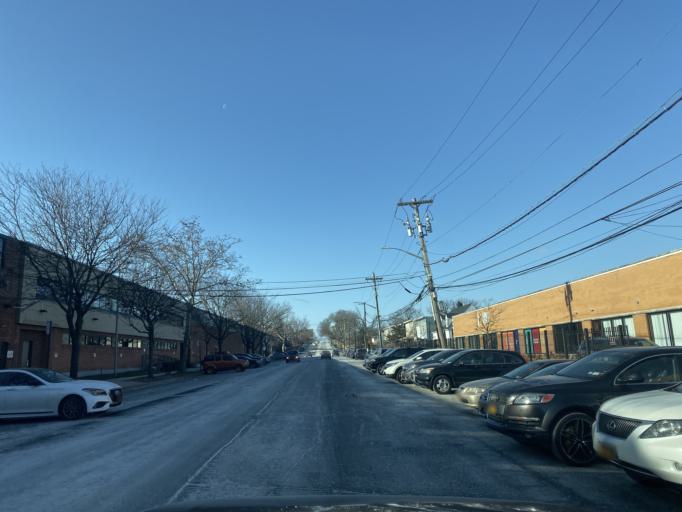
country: US
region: New York
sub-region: Bronx
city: The Bronx
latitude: 40.8240
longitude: -73.8438
